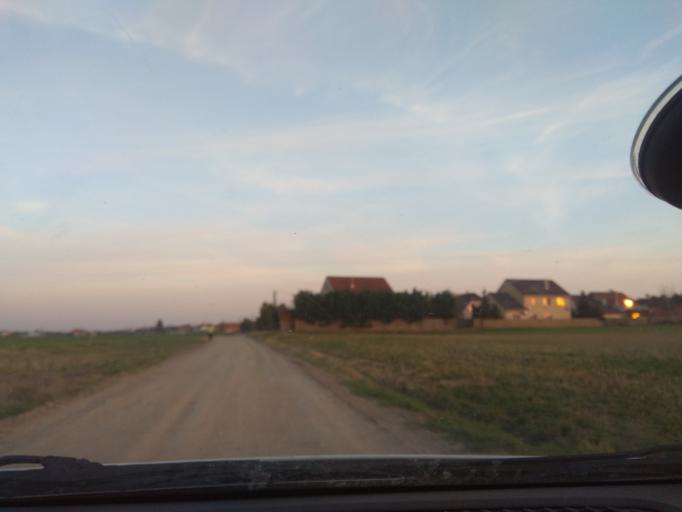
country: HU
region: Pest
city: Szigetszentmiklos
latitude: 47.3597
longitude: 19.0347
